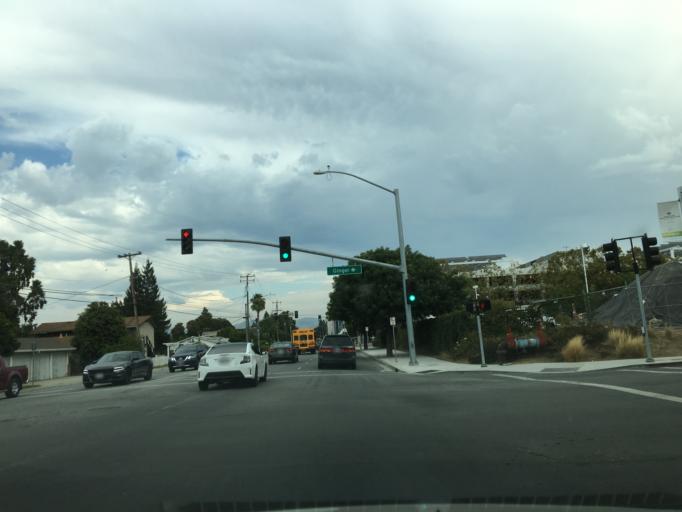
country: US
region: California
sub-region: Santa Clara County
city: Burbank
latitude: 37.3161
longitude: -121.9364
